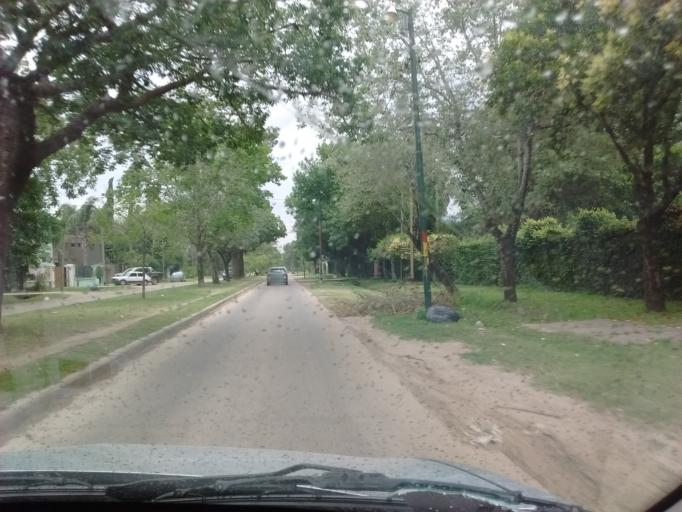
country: AR
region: Santa Fe
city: Funes
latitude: -32.9165
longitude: -60.7990
